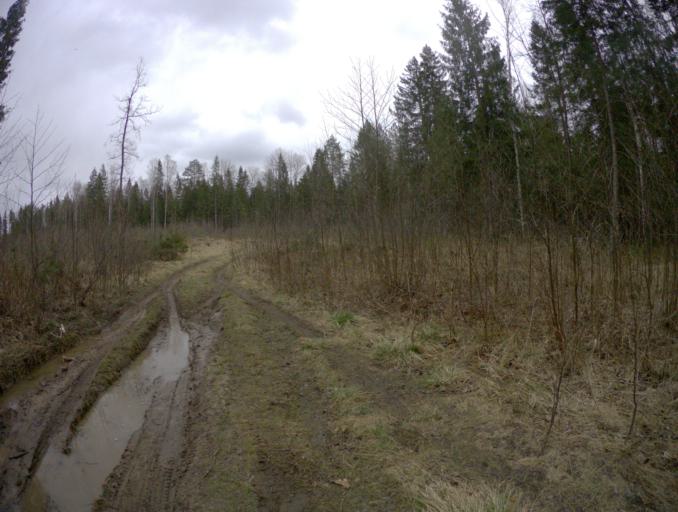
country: RU
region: Vladimir
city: Sudogda
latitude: 56.0265
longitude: 40.7968
